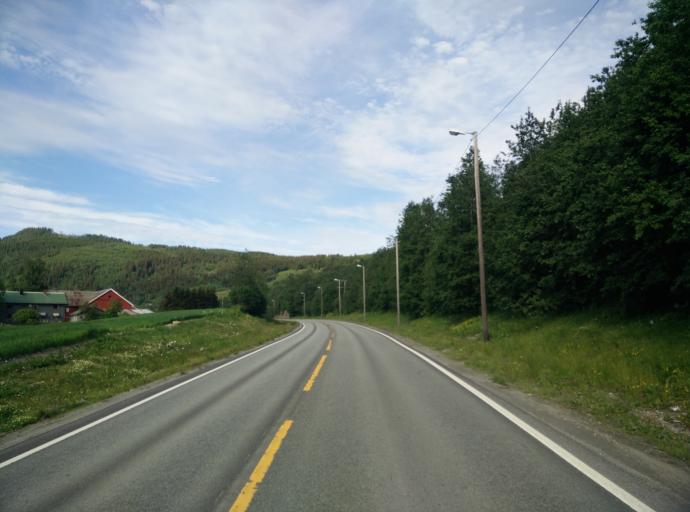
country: NO
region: Sor-Trondelag
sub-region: Orkdal
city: Orkanger
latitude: 63.2792
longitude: 9.8402
